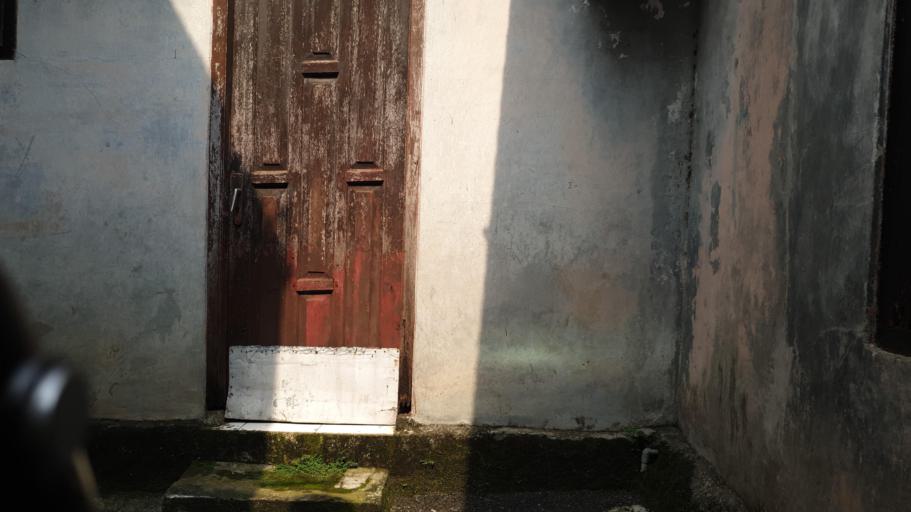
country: ID
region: West Java
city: Depok
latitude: -6.3323
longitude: 106.8252
